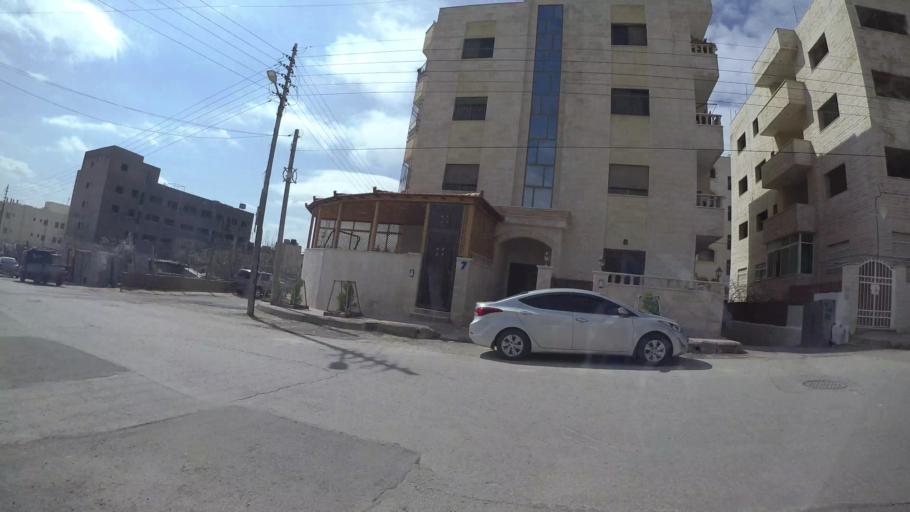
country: JO
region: Amman
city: Wadi as Sir
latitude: 31.9494
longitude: 35.8309
